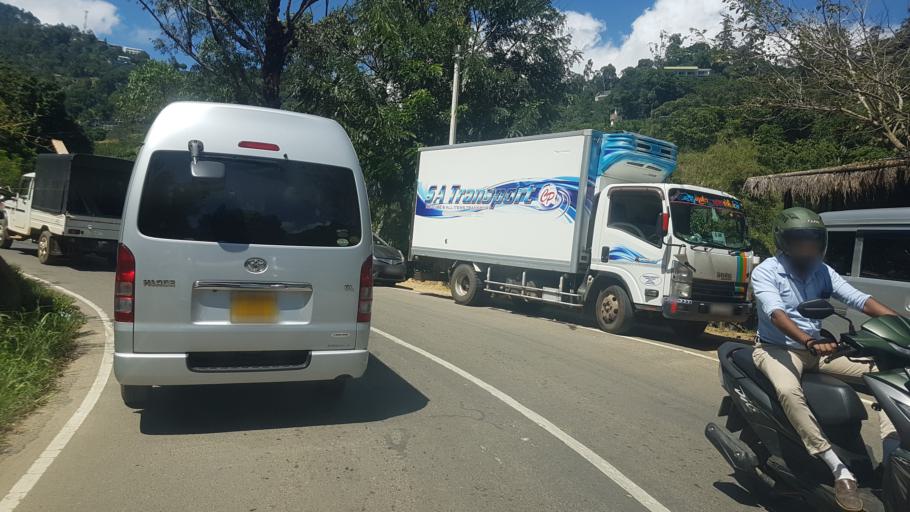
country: LK
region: Uva
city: Badulla
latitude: 6.8670
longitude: 81.0504
